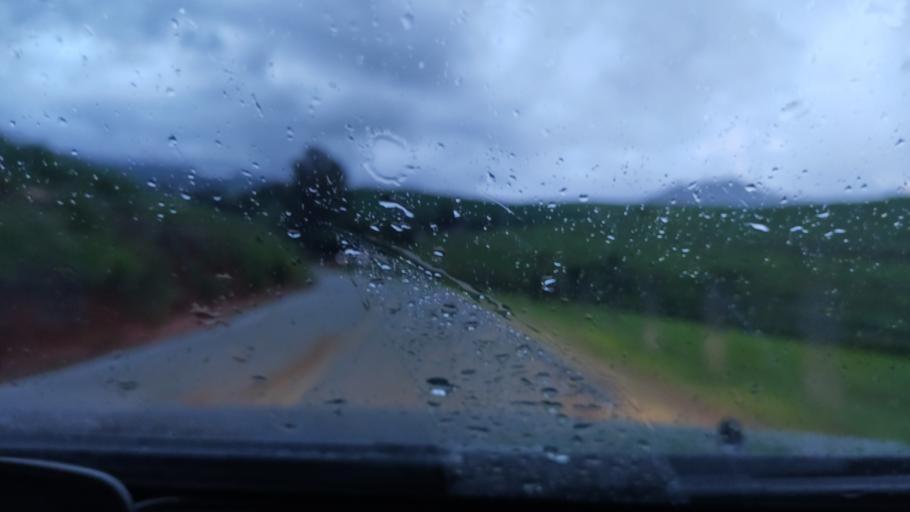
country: BR
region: Sao Paulo
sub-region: Aguas De Lindoia
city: Aguas de Lindoia
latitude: -22.5656
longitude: -46.6227
